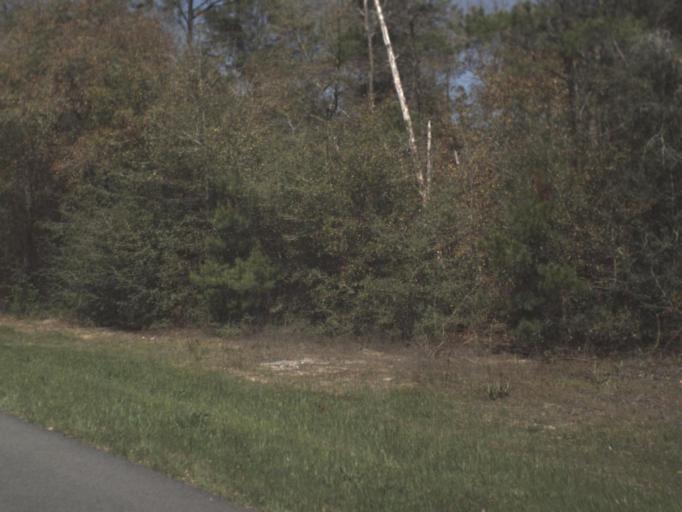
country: US
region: Florida
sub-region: Walton County
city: DeFuniak Springs
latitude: 30.7481
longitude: -86.2386
